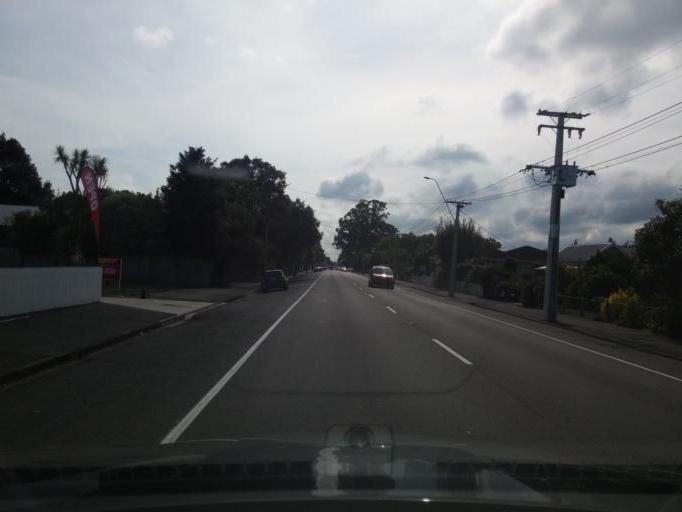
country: NZ
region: Wellington
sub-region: Masterton District
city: Masterton
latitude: -41.0845
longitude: 175.4558
